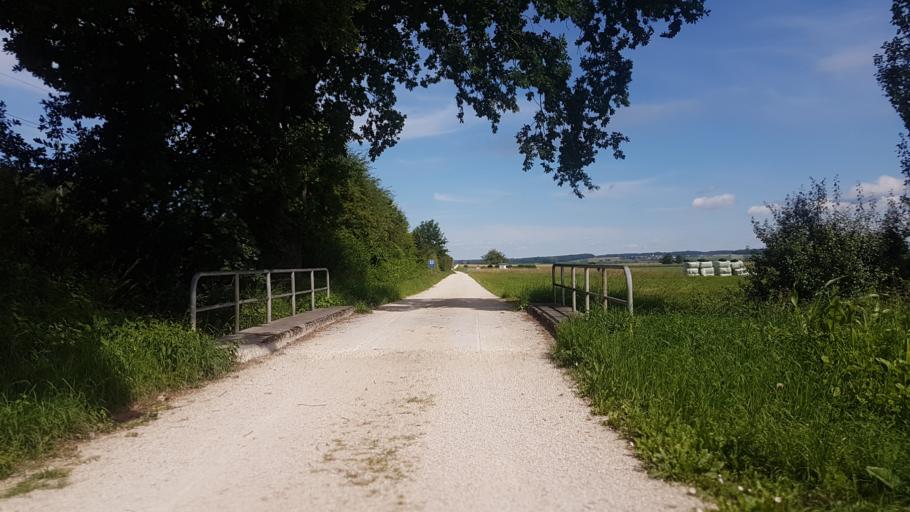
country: DE
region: Bavaria
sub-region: Regierungsbezirk Mittelfranken
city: Markt Berolzheim
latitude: 49.0190
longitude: 10.8517
